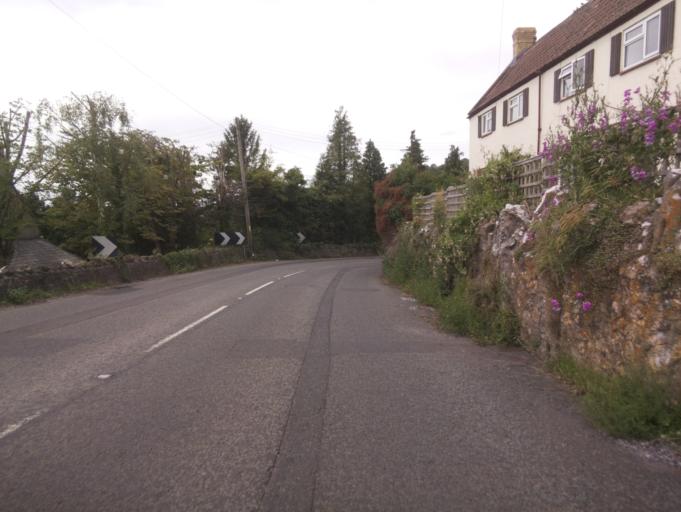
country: GB
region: England
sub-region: Somerset
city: Bradley Cross
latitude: 51.2463
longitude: -2.7370
